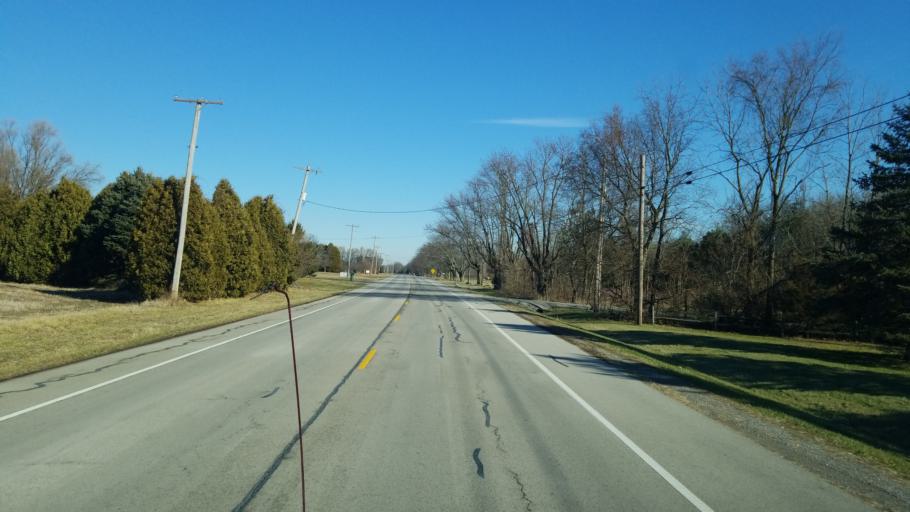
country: US
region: Ohio
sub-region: Lucas County
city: Whitehouse
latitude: 41.4411
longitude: -83.8105
